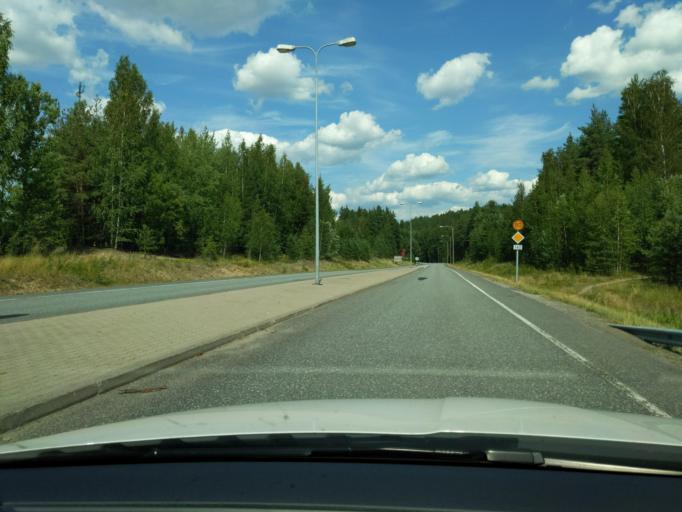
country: FI
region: Paijanne Tavastia
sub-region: Lahti
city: Heinola
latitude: 61.2604
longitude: 26.0683
